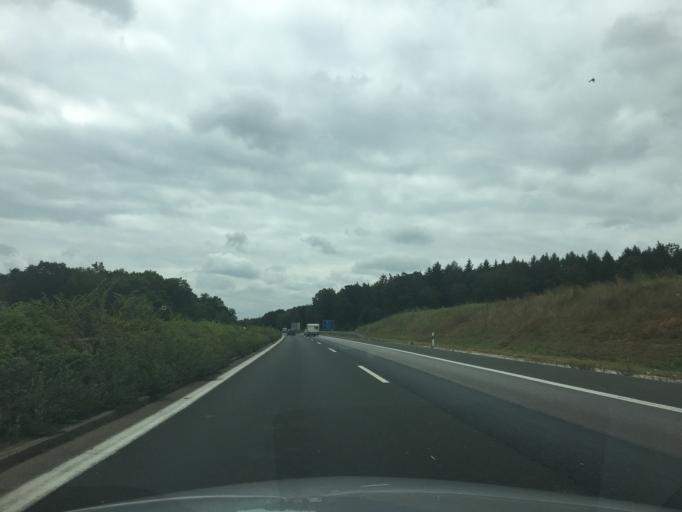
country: DE
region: Bavaria
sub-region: Regierungsbezirk Mittelfranken
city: Herzogenaurach
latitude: 49.5802
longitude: 10.9289
